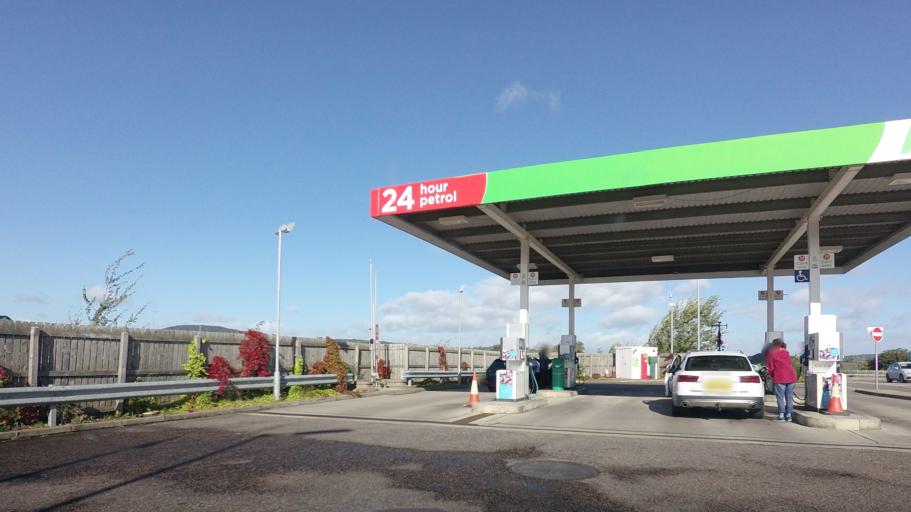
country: GB
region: Scotland
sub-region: Highland
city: Inverness
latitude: 57.4503
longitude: -4.2168
